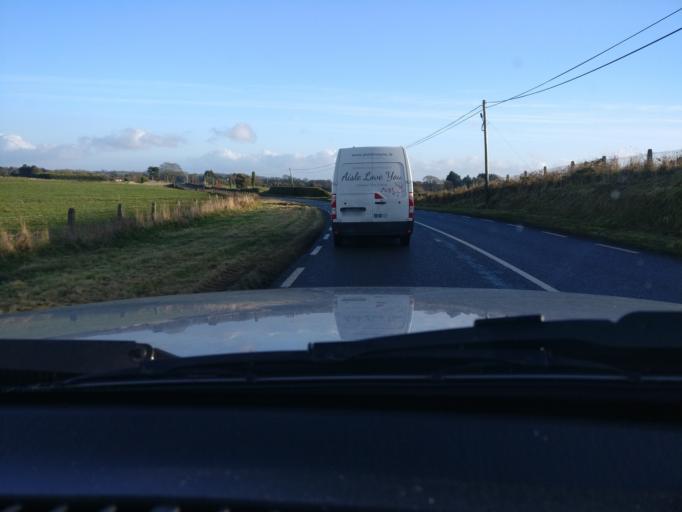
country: IE
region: Ulster
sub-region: An Cabhan
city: Mullagh
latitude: 53.7222
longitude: -6.9813
